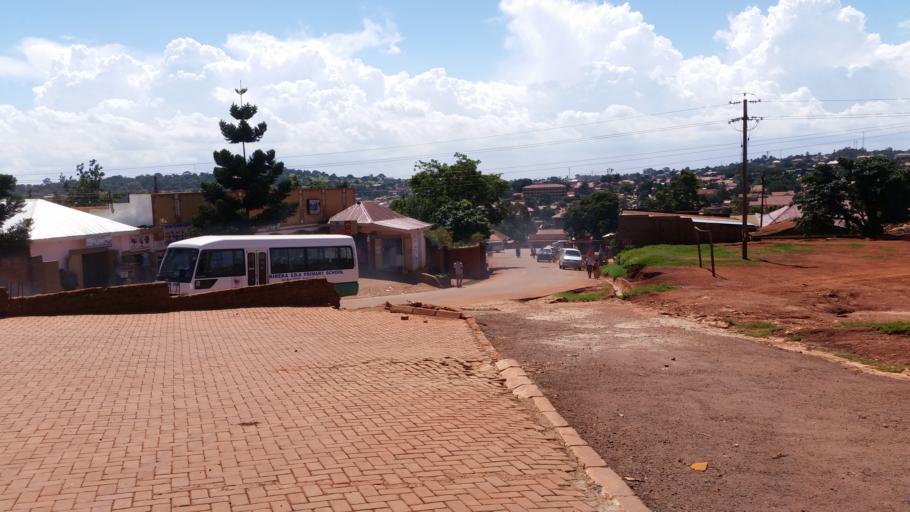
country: UG
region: Central Region
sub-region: Wakiso District
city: Kireka
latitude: 0.3419
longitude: 32.6457
